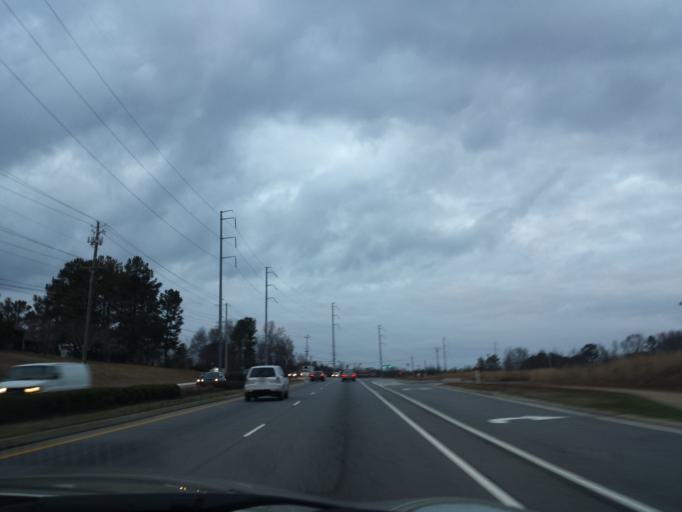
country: US
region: Georgia
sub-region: Fulton County
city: Johns Creek
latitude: 34.0377
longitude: -84.1850
